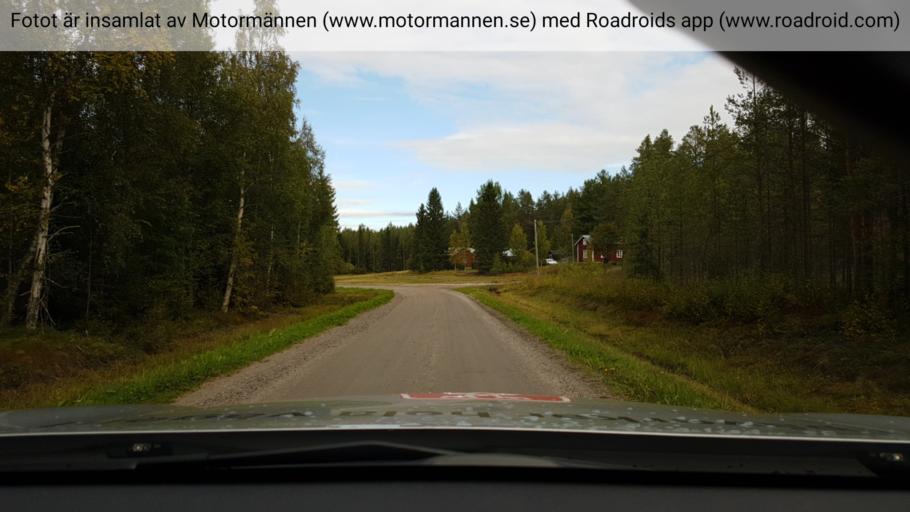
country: SE
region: Vaesterbotten
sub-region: Skelleftea Kommun
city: Backa
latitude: 65.1547
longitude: 21.1611
